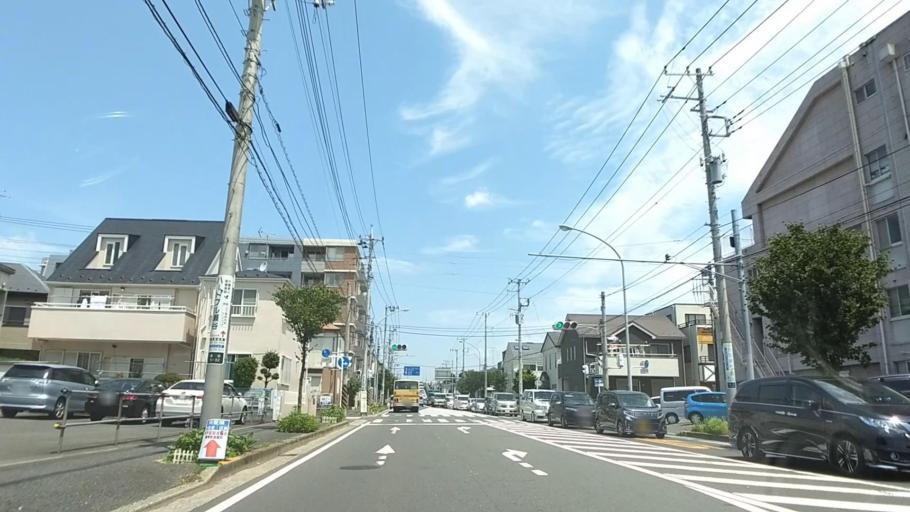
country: JP
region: Kanagawa
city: Minami-rinkan
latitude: 35.4668
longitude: 139.4800
